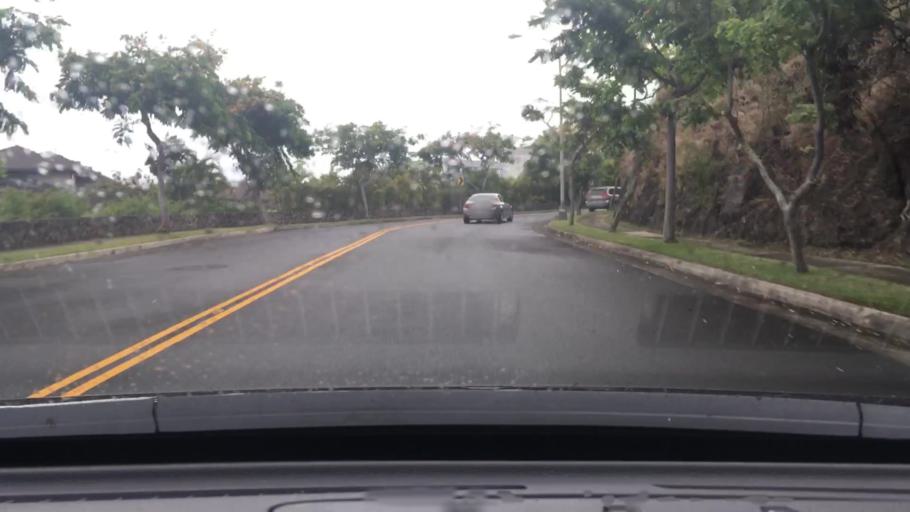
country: US
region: Hawaii
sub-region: Honolulu County
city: Waimanalo Beach
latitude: 21.2892
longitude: -157.7026
